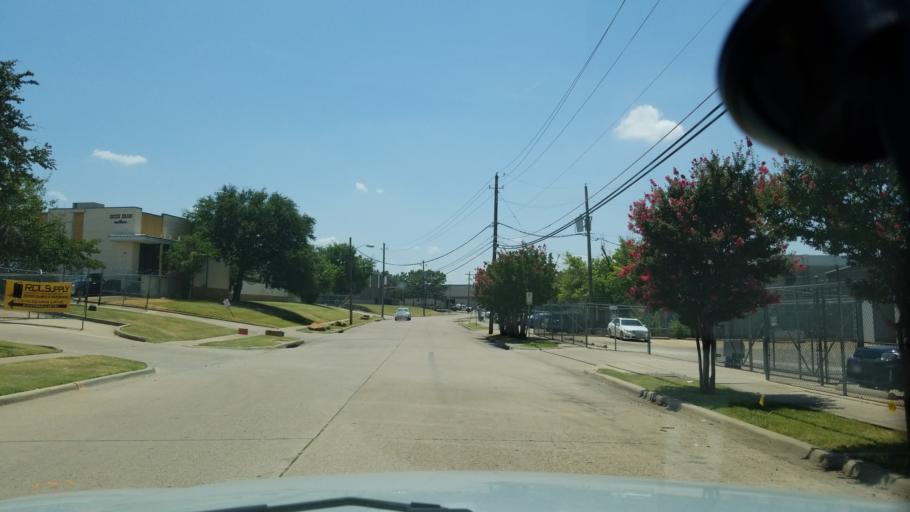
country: US
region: Texas
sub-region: Dallas County
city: Farmers Branch
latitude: 32.8925
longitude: -96.8844
